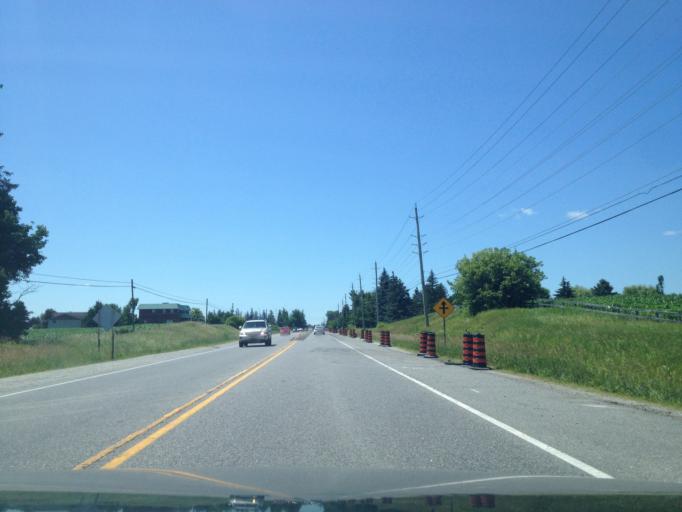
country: CA
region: Ontario
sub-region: Halton
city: Milton
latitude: 43.6493
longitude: -80.0152
